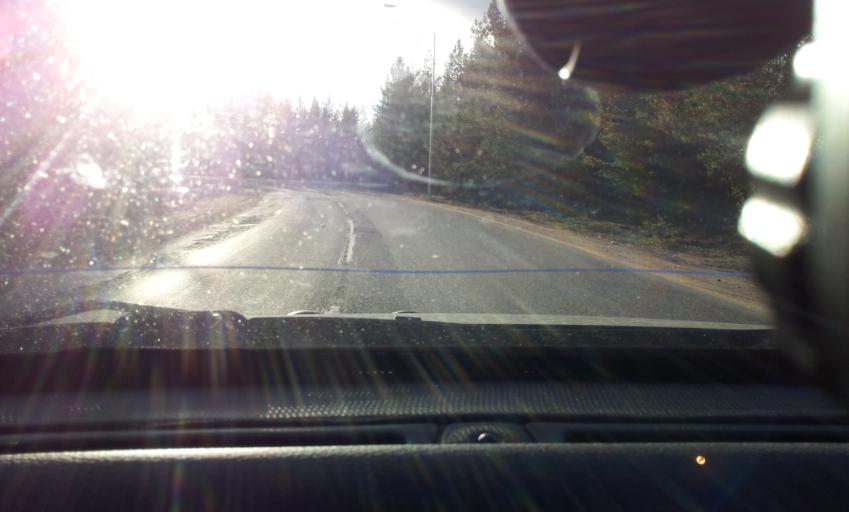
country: SE
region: Jaemtland
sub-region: Harjedalens Kommun
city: Sveg
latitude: 62.1290
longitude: 14.9746
